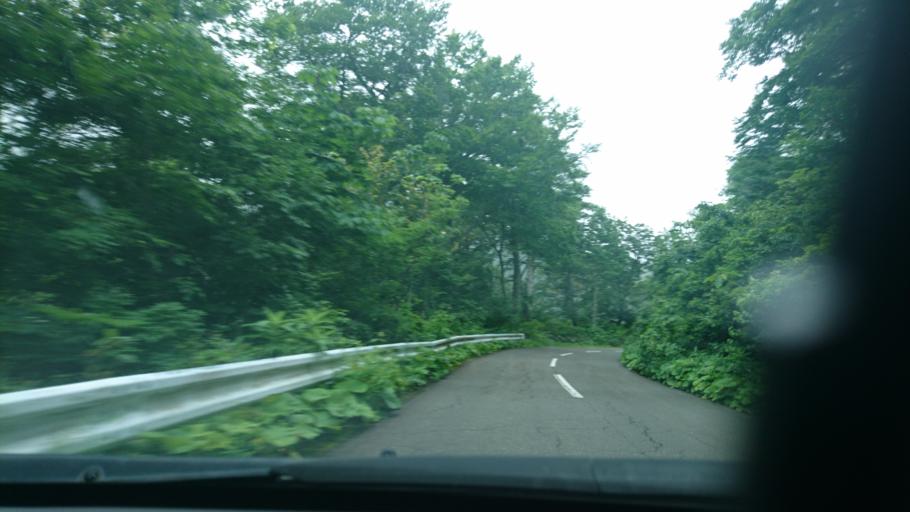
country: JP
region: Akita
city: Yuzawa
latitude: 39.1443
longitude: 140.7677
